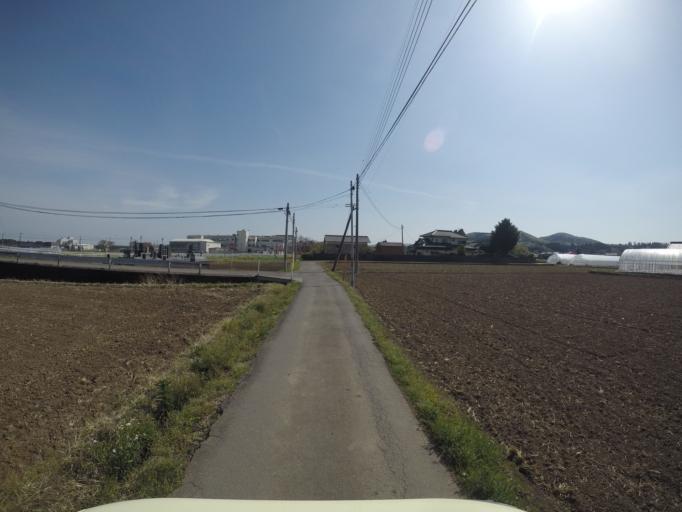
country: JP
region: Tochigi
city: Tochigi
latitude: 36.4436
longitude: 139.7213
